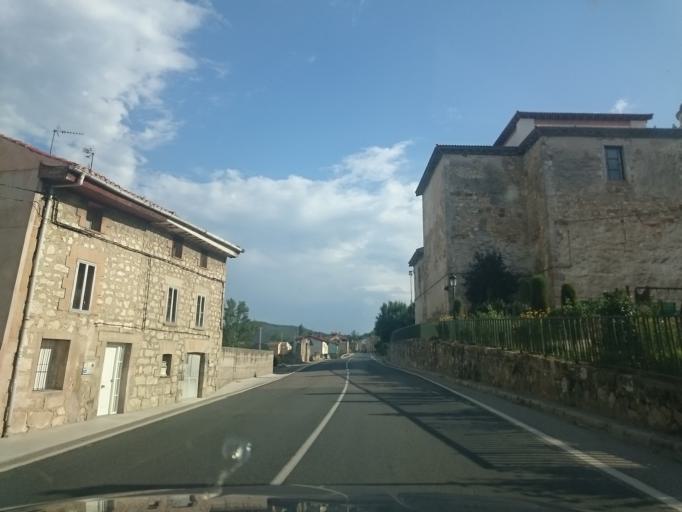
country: ES
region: Castille and Leon
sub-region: Provincia de Burgos
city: Espinosa del Camino
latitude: 42.3891
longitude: -3.3087
